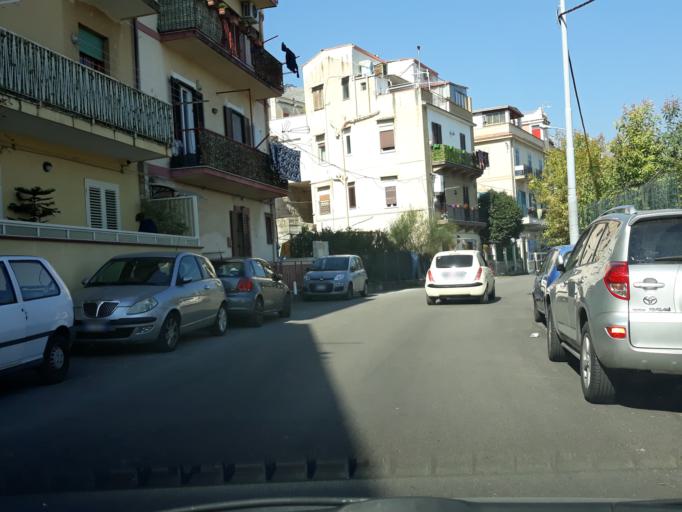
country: IT
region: Sicily
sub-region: Palermo
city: Piano dei Geli
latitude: 38.1142
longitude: 13.2953
